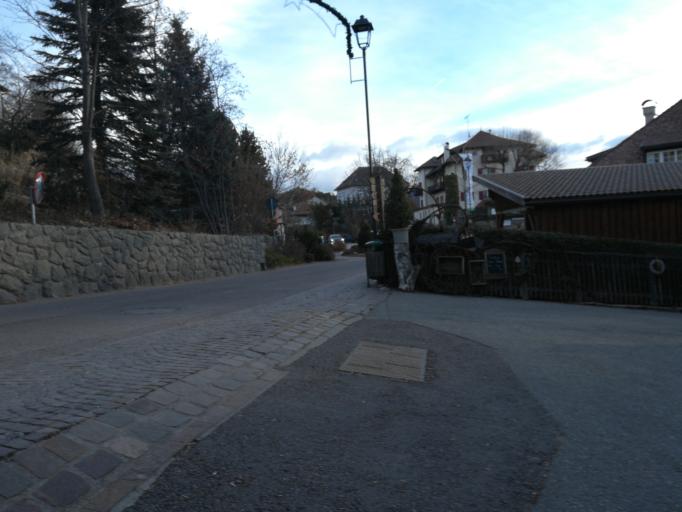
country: IT
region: Trentino-Alto Adige
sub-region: Bolzano
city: Collalbo
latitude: 46.5371
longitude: 11.4617
